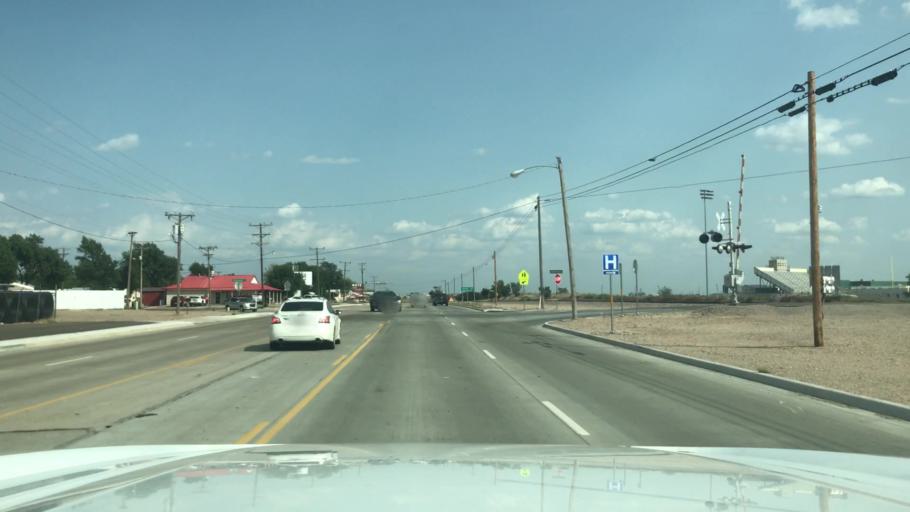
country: US
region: Texas
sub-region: Dallam County
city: Dalhart
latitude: 36.0513
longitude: -102.5013
